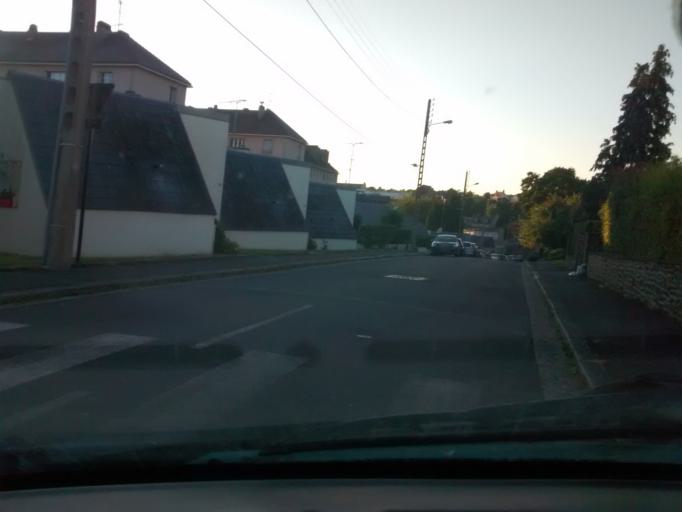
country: FR
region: Lower Normandy
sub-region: Departement de la Manche
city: Saint-Lo
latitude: 49.1113
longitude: -1.0806
